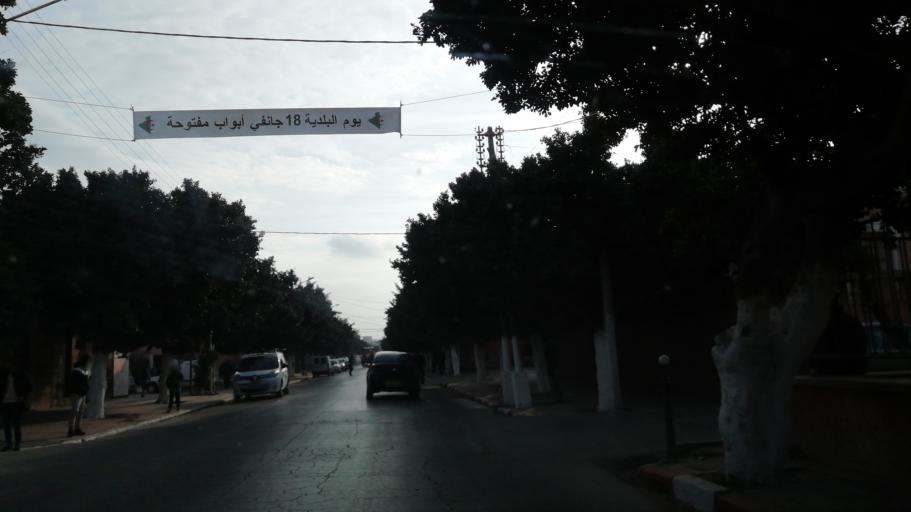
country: DZ
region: Mostaganem
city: Mostaganem
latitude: 35.8618
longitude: 0.0736
